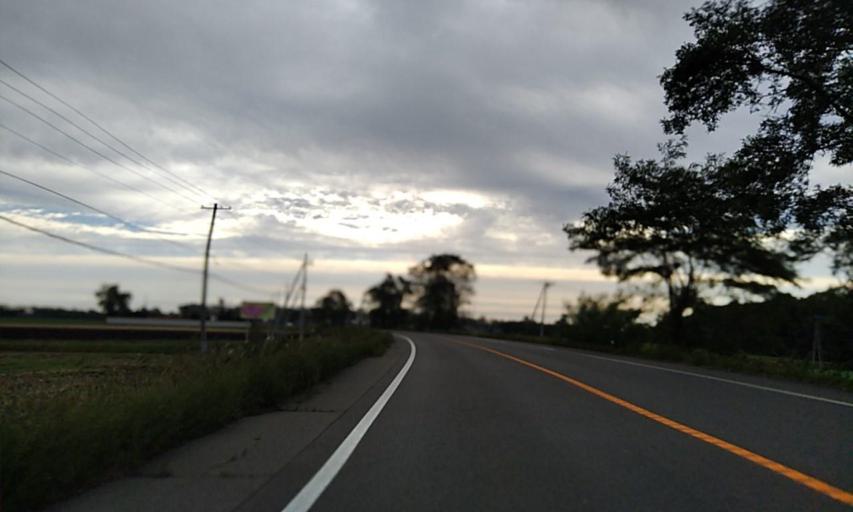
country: JP
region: Hokkaido
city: Obihiro
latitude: 42.9180
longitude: 142.9998
